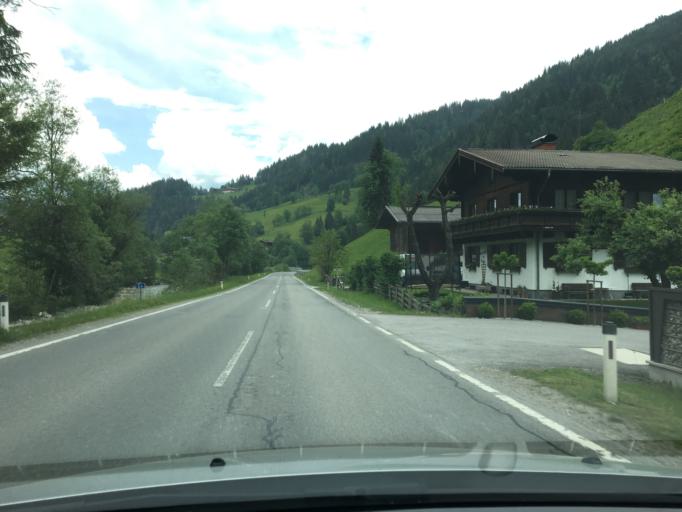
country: AT
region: Salzburg
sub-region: Politischer Bezirk Sankt Johann im Pongau
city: Wagrain
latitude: 47.3150
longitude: 13.3042
